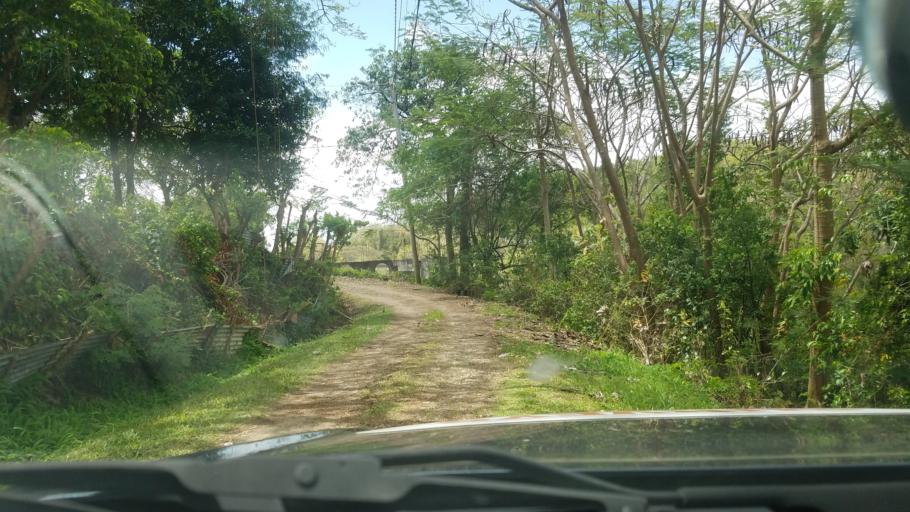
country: LC
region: Gros-Islet
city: Gros Islet
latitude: 14.0593
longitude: -60.9515
